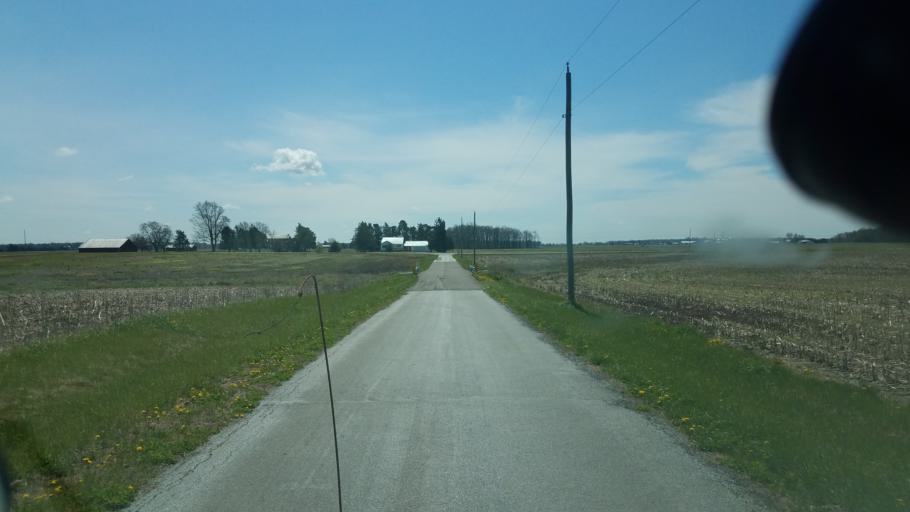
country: US
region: Ohio
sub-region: Hardin County
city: Kenton
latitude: 40.6748
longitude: -83.5051
